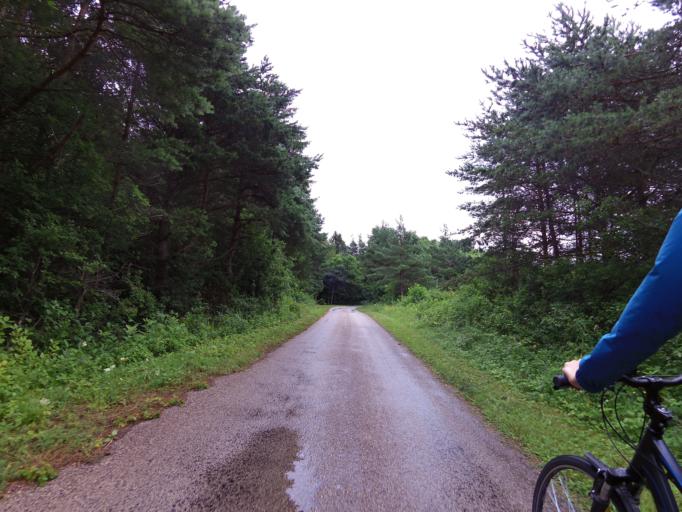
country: EE
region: Laeaene
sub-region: Vormsi vald
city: Hullo
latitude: 59.0189
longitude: 23.3339
